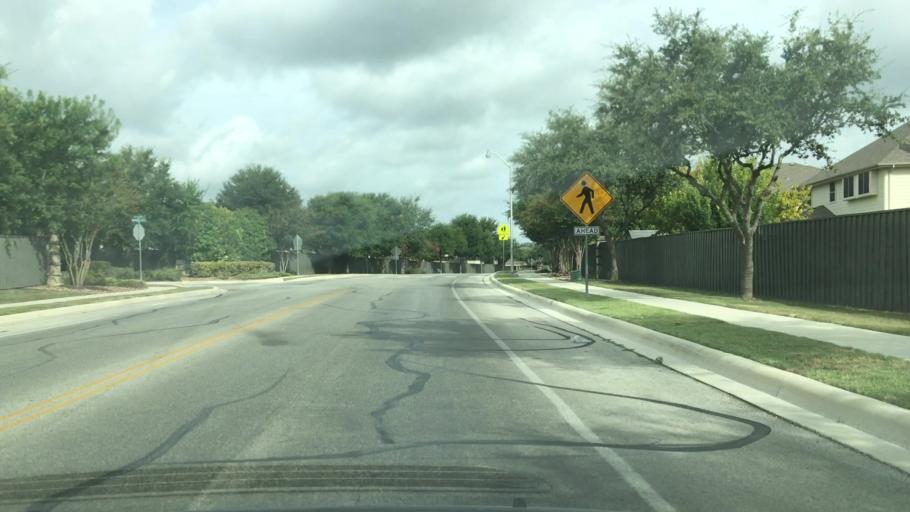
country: US
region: Texas
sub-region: Guadalupe County
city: Cibolo
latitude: 29.5769
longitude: -98.2380
